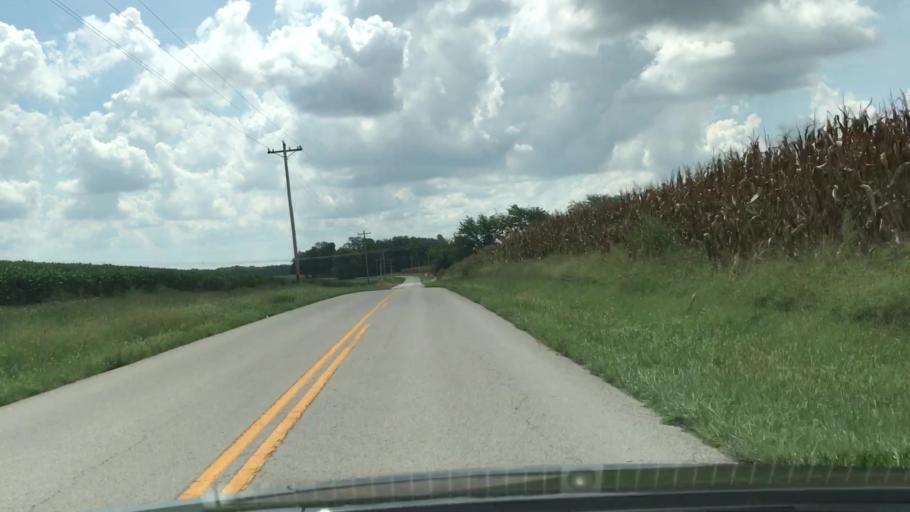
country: US
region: Kentucky
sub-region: Todd County
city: Elkton
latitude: 36.7756
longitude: -87.1189
